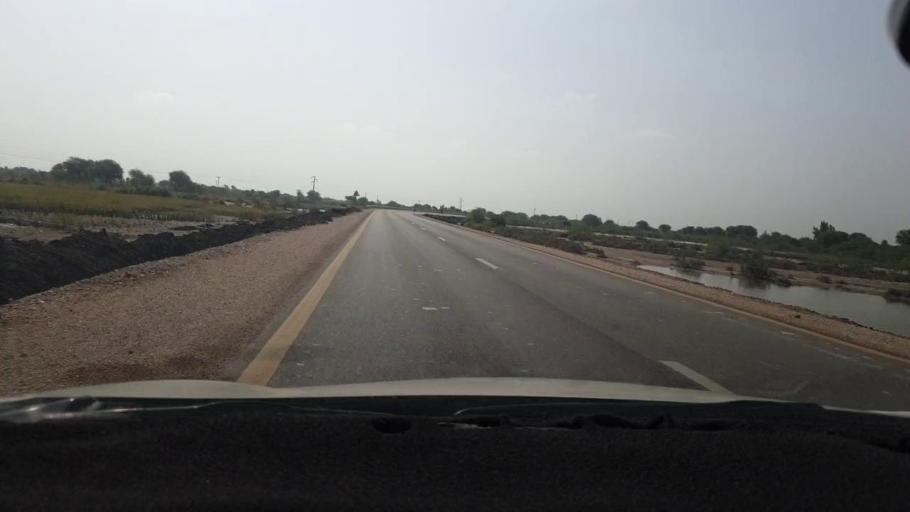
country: PK
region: Sindh
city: Jhol
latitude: 25.8591
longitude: 69.0582
